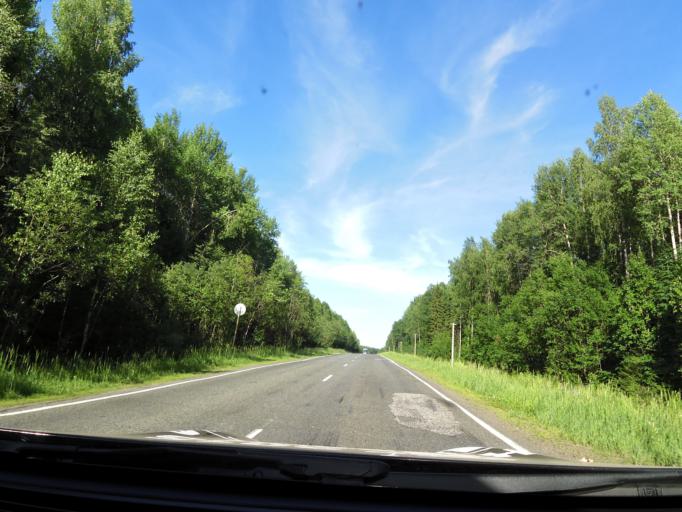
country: RU
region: Kirov
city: Belaya Kholunitsa
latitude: 58.9172
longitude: 51.0973
